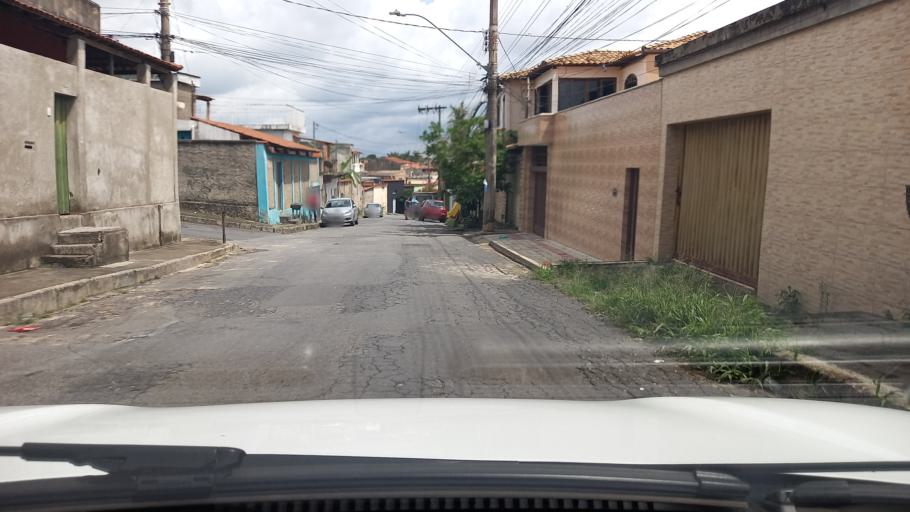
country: BR
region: Minas Gerais
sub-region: Contagem
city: Contagem
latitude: -19.9033
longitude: -44.0261
